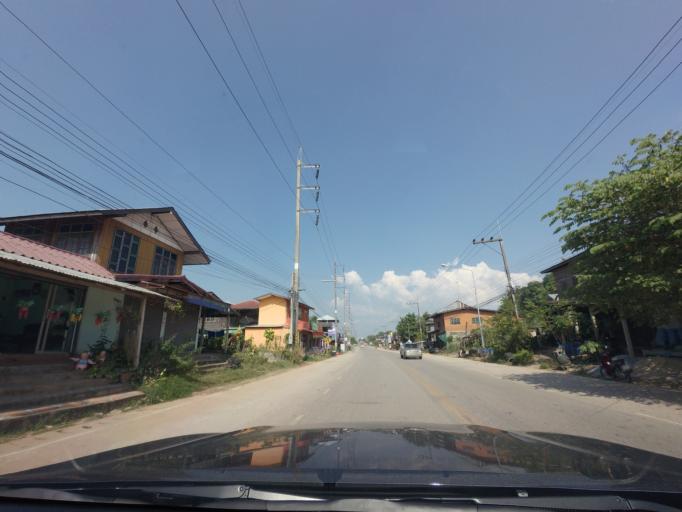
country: TH
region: Phitsanulok
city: Nakhon Thai
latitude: 17.1119
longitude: 100.8571
